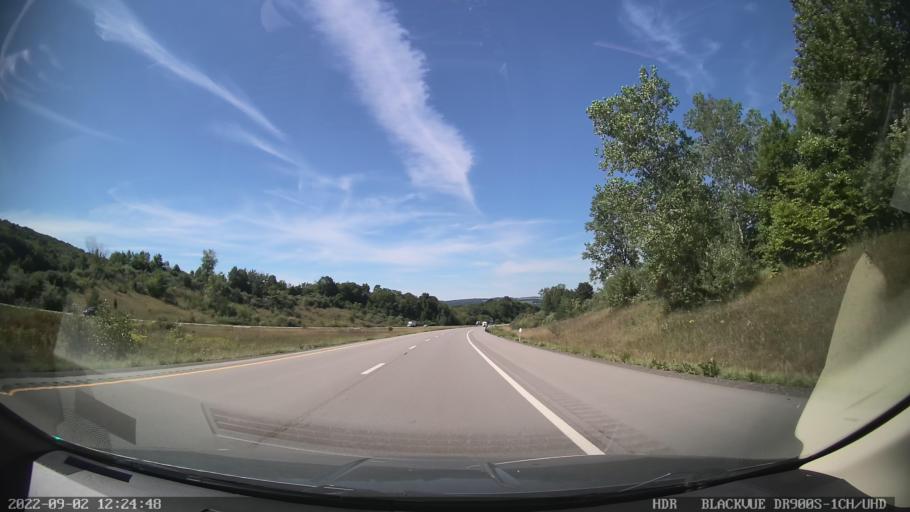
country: US
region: New York
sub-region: Livingston County
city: Dansville
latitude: 42.5297
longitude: -77.6525
